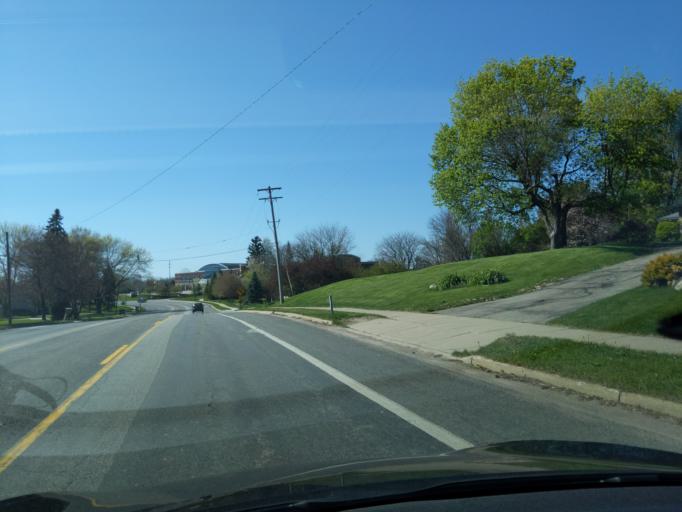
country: US
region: Michigan
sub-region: Kent County
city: East Grand Rapids
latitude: 42.9258
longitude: -85.5656
